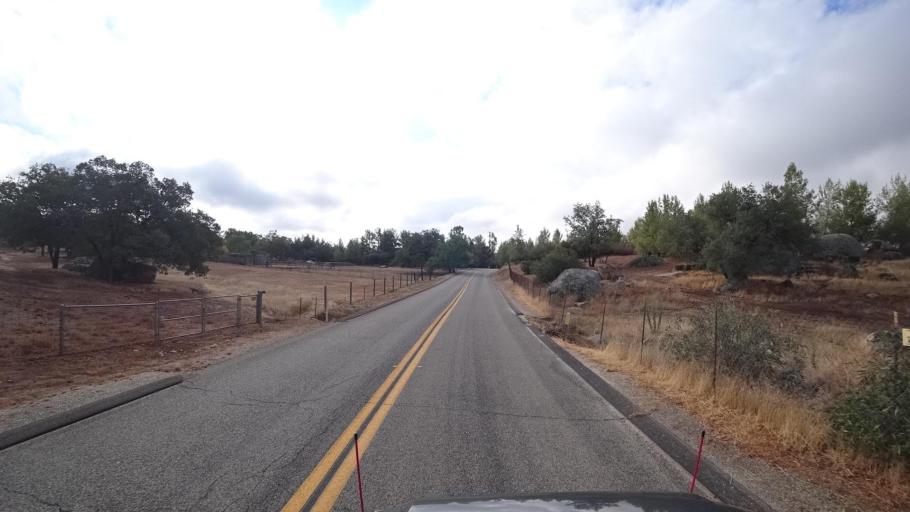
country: MX
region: Baja California
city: Tecate
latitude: 32.6375
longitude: -116.6357
